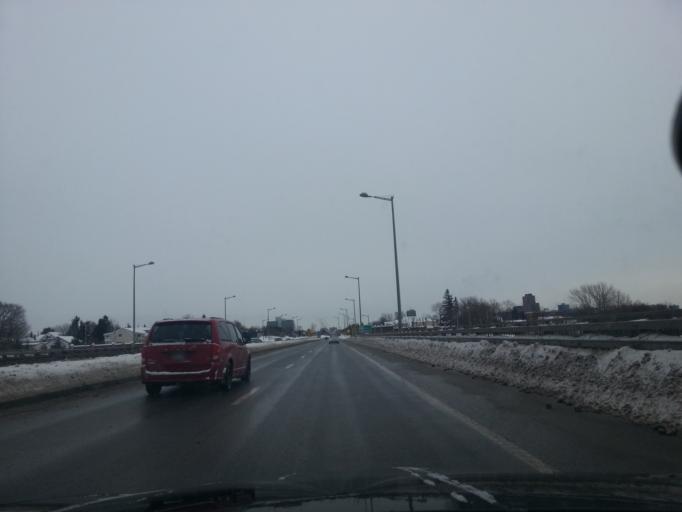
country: CA
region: Ontario
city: Ottawa
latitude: 45.4324
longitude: -75.7463
